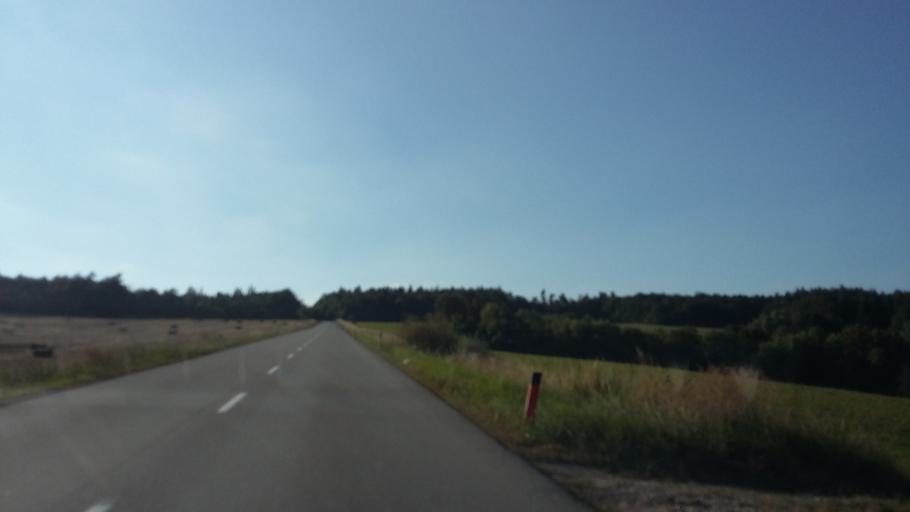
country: CZ
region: South Moravian
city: Ricany
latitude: 49.2172
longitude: 16.3799
